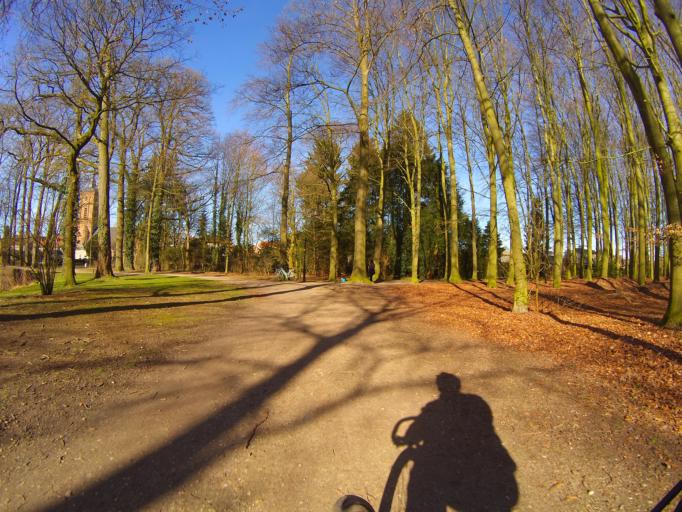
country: NL
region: Utrecht
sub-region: Gemeente Utrechtse Heuvelrug
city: Overberg
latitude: 52.0782
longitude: 5.4900
